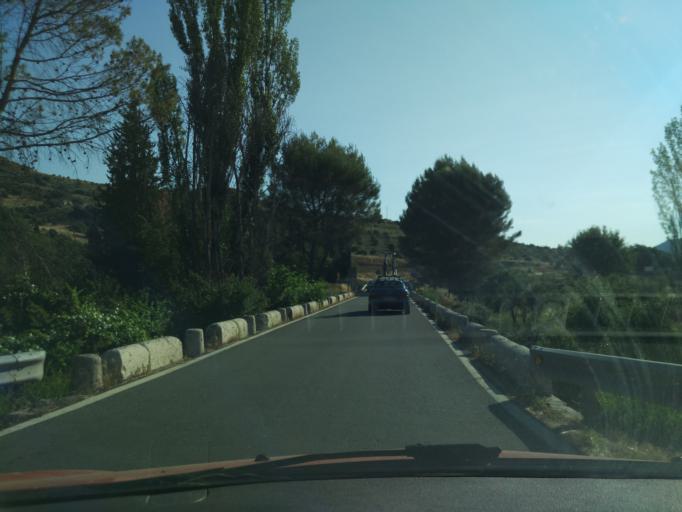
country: ES
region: Madrid
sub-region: Provincia de Madrid
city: Ambite
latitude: 40.3182
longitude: -3.1970
